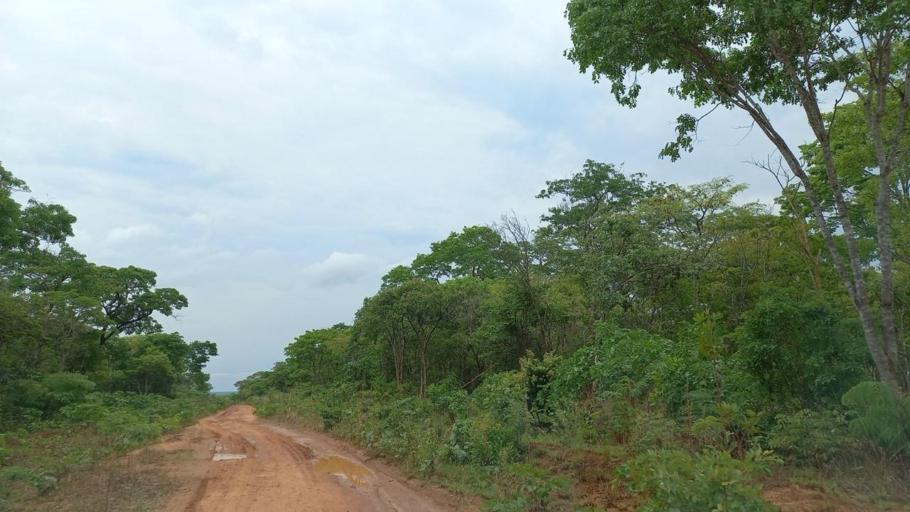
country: ZM
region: North-Western
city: Kalengwa
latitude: -13.6169
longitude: 24.9761
